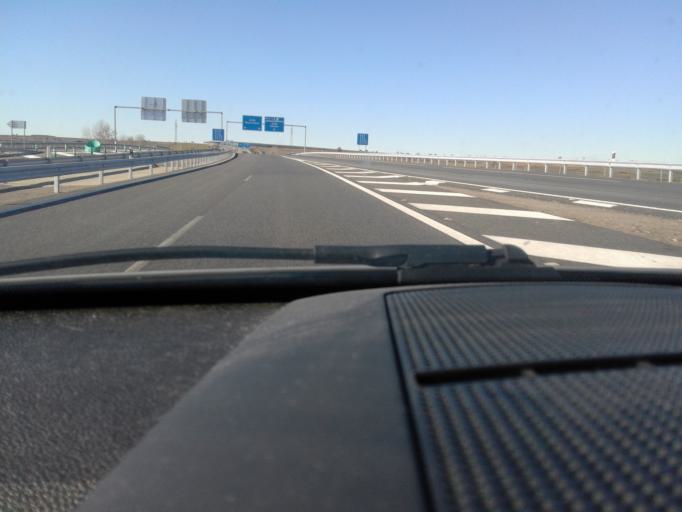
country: ES
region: Castille and Leon
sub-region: Provincia de Leon
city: Onzonilla
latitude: 42.5051
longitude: -5.5810
